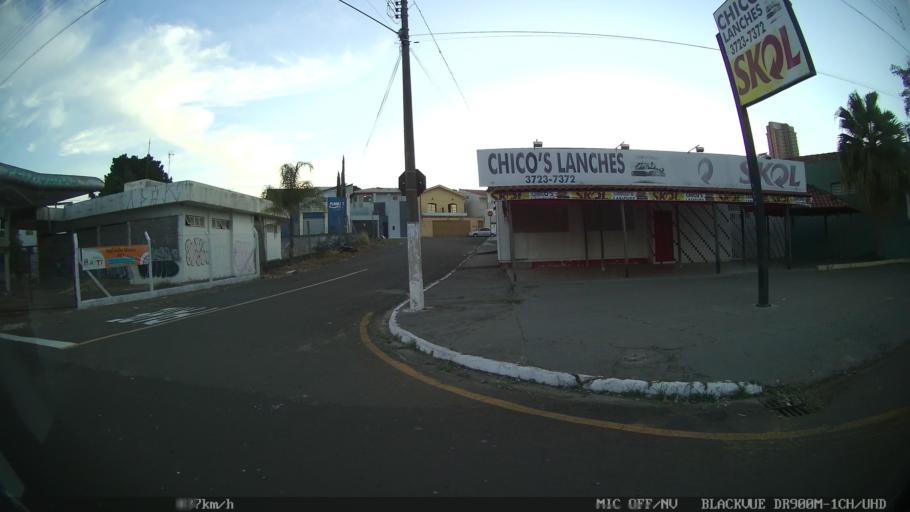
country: BR
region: Sao Paulo
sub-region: Franca
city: Franca
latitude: -20.5397
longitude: -47.4082
